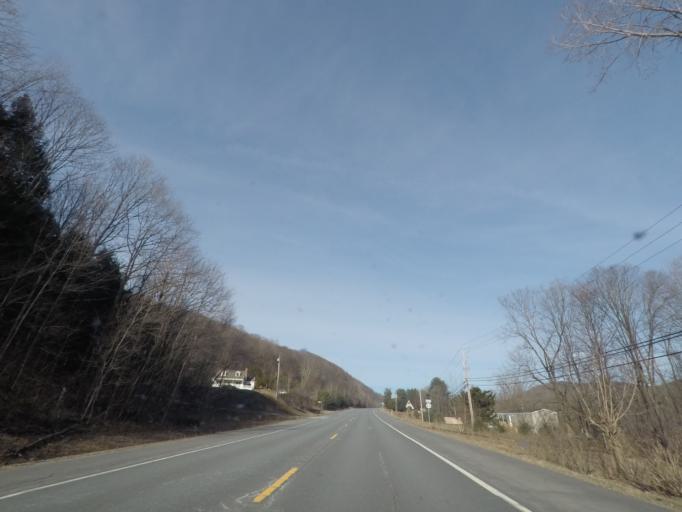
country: US
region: Massachusetts
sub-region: Berkshire County
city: Williamstown
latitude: 42.7188
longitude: -73.3722
